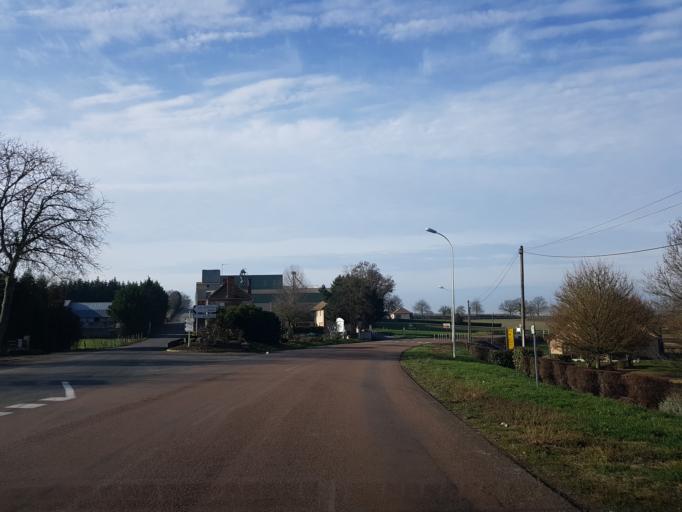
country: FR
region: Bourgogne
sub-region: Departement de Saone-et-Loire
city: Bourbon-Lancy
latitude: 46.5991
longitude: 3.8446
